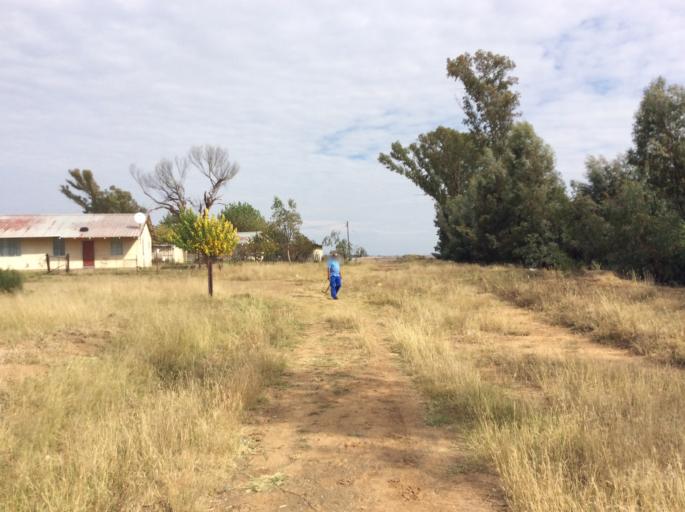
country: LS
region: Mafeteng
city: Mafeteng
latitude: -29.7280
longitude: 27.0262
